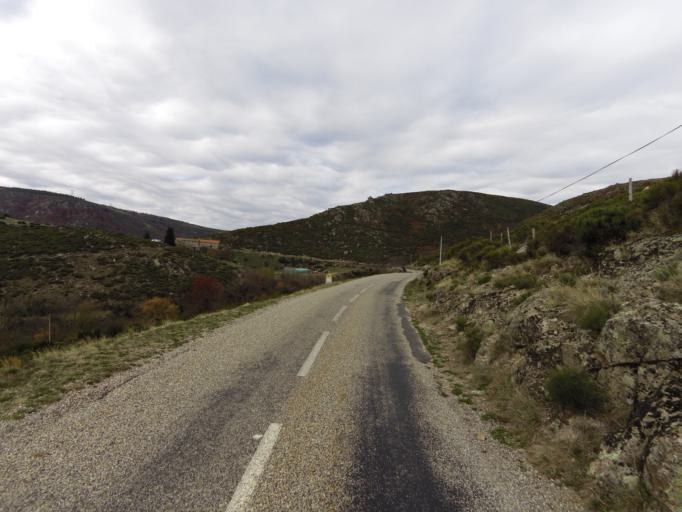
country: FR
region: Rhone-Alpes
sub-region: Departement de l'Ardeche
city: Les Vans
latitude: 44.5144
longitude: 4.0338
